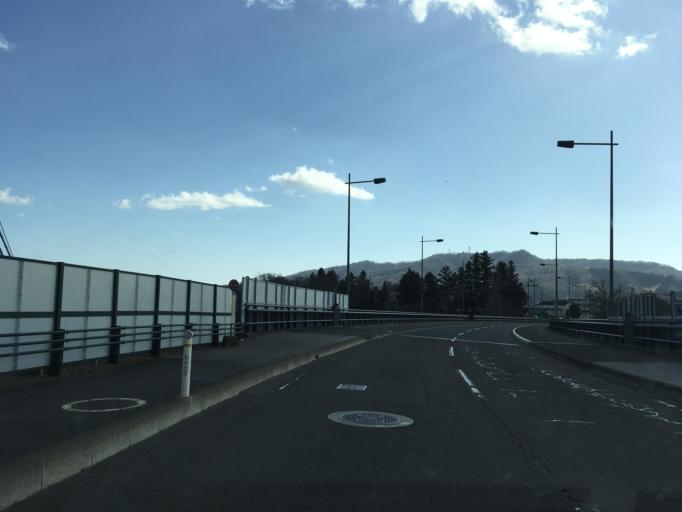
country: JP
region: Miyagi
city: Sendai
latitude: 38.2795
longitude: 140.7633
